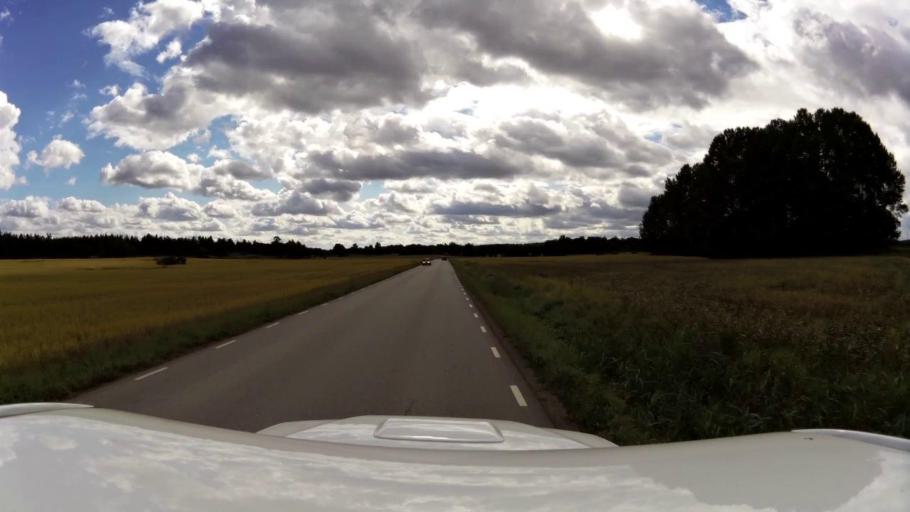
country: SE
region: OEstergoetland
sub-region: Linkopings Kommun
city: Linkoping
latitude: 58.3788
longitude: 15.5944
